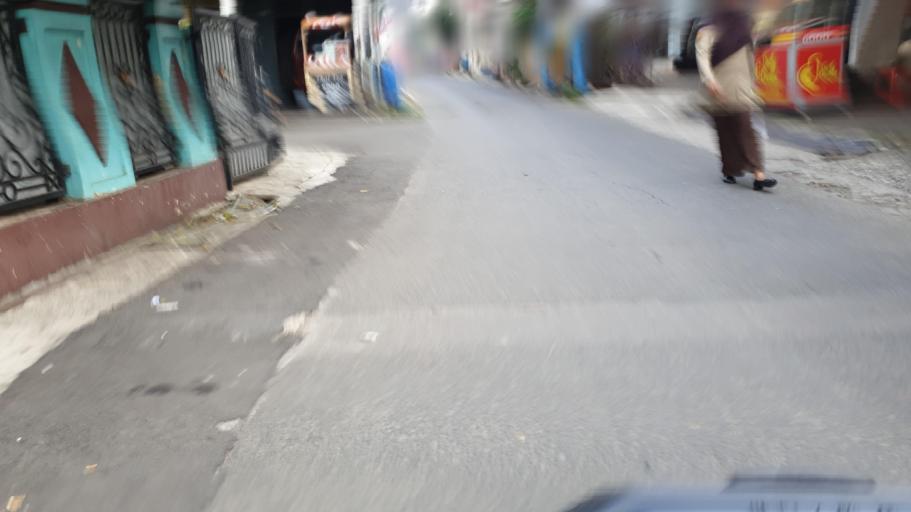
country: ID
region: West Java
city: Depok
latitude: -6.3691
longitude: 106.8515
